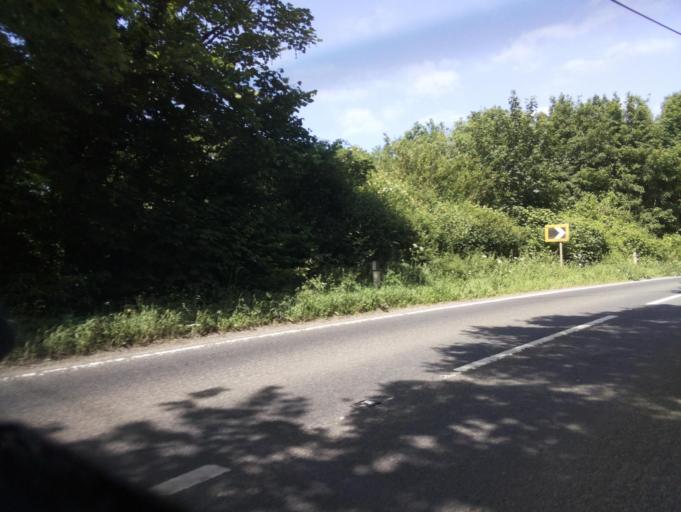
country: GB
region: England
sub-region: Somerset
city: Redlynch
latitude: 51.0585
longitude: -2.4555
